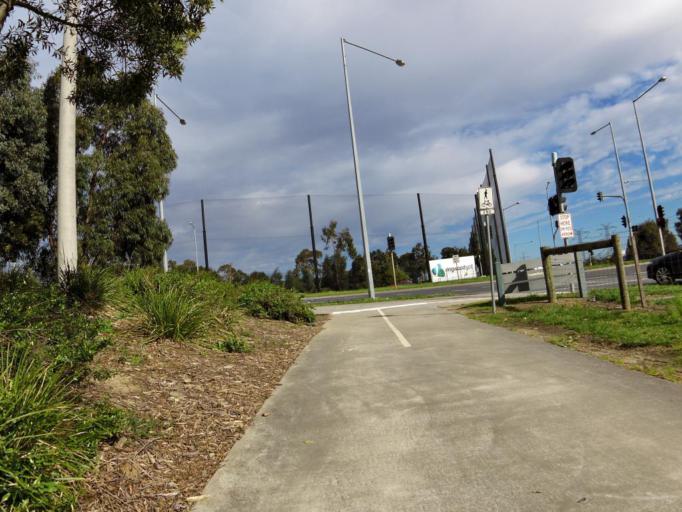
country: AU
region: Victoria
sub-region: Knox
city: Wantirna
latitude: -37.8320
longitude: 145.2184
